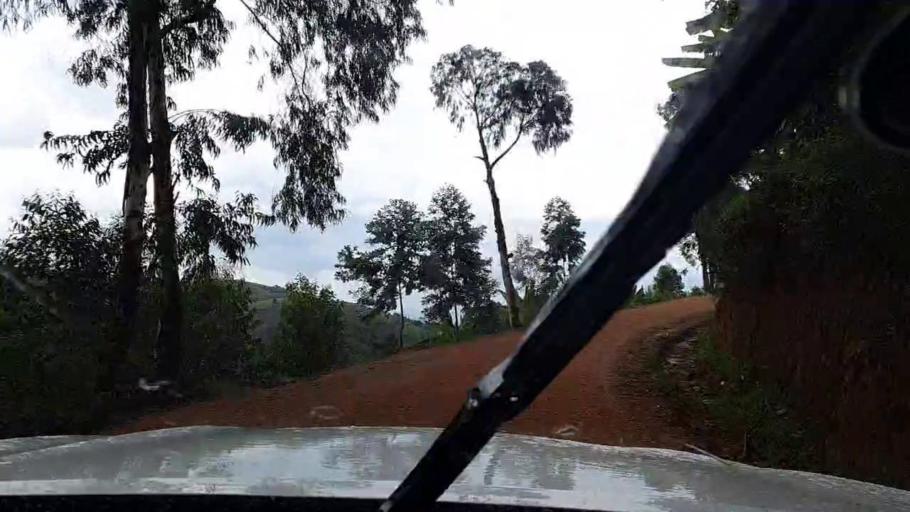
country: RW
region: Western Province
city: Kibuye
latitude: -2.1478
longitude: 29.4246
